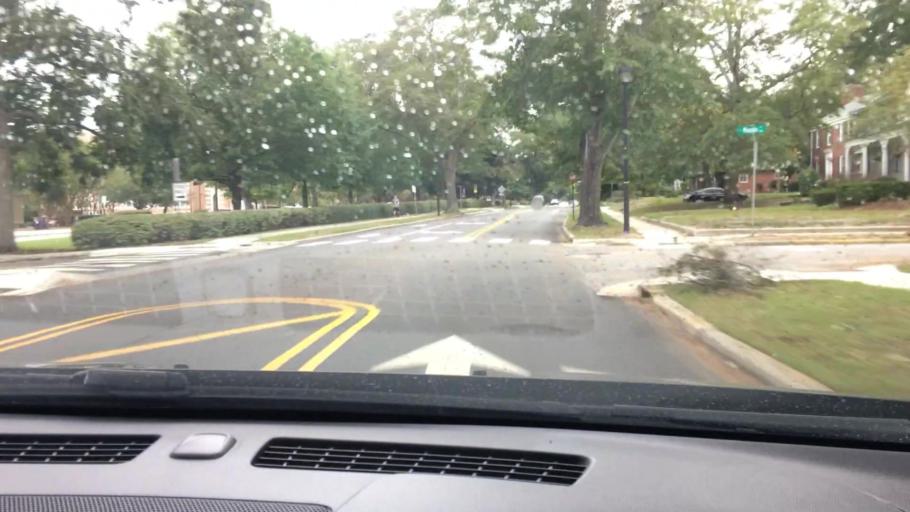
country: US
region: North Carolina
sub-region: Pitt County
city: Greenville
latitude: 35.6068
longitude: -77.3607
